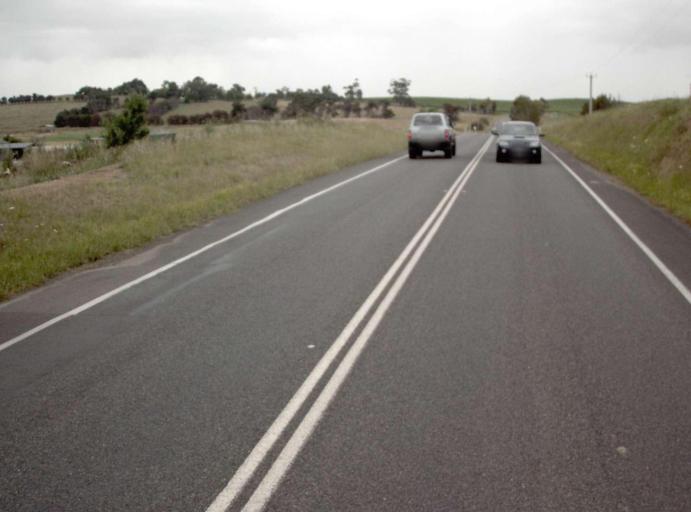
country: AU
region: Victoria
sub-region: Yarra Ranges
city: Yarra Glen
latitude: -37.6264
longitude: 145.4087
